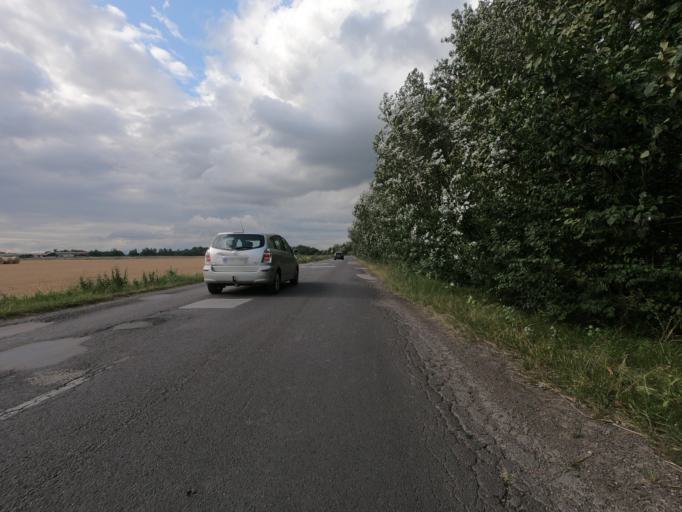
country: HU
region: Heves
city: Poroszlo
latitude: 47.6678
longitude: 20.6626
